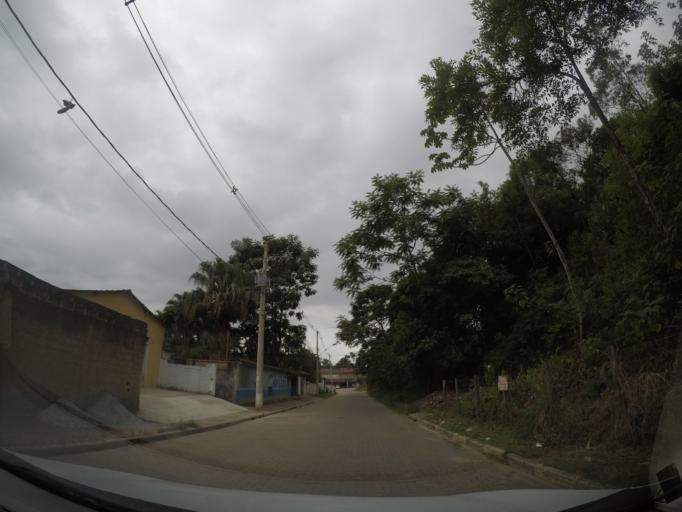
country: BR
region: Sao Paulo
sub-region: Aruja
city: Aruja
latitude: -23.3643
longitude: -46.4042
